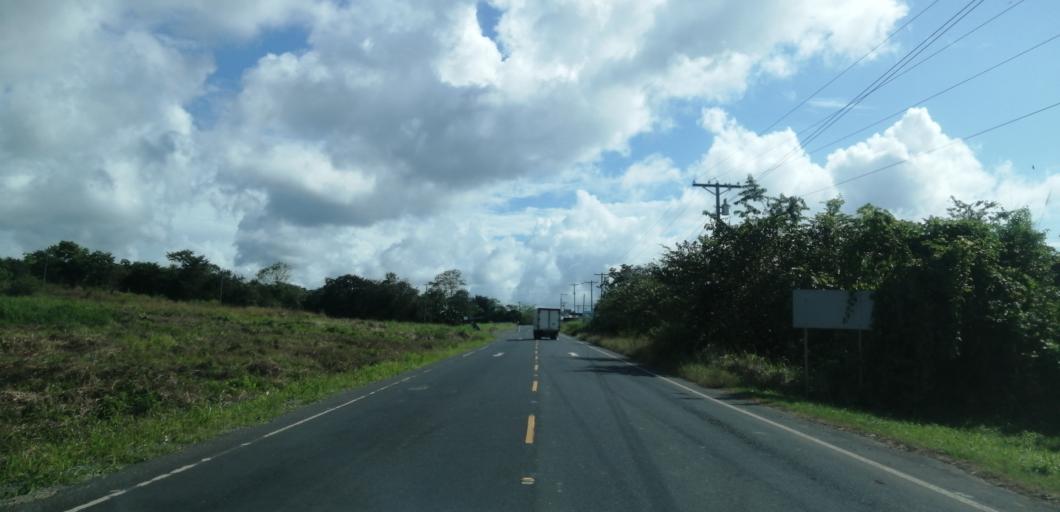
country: PA
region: Panama
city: Canita
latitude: 9.2209
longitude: -78.8994
